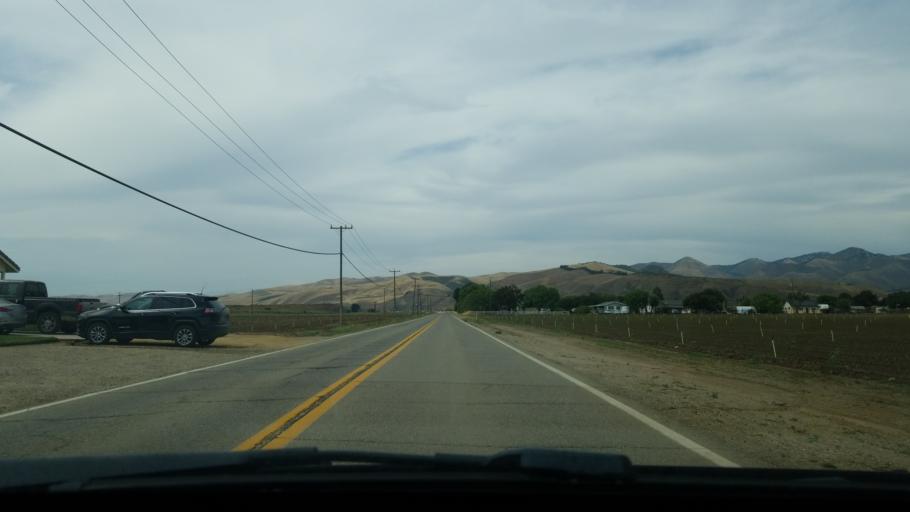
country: US
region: California
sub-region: Santa Barbara County
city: Orcutt
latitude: 34.8907
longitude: -120.3150
